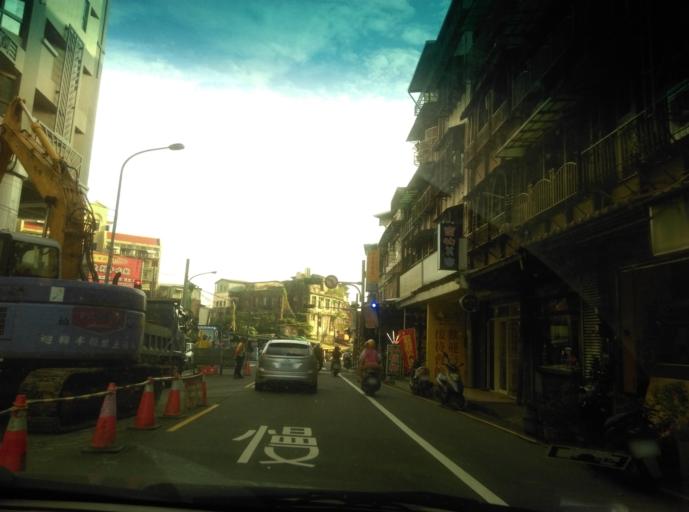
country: TW
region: Taiwan
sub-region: Keelung
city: Keelung
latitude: 25.1466
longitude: 121.7385
